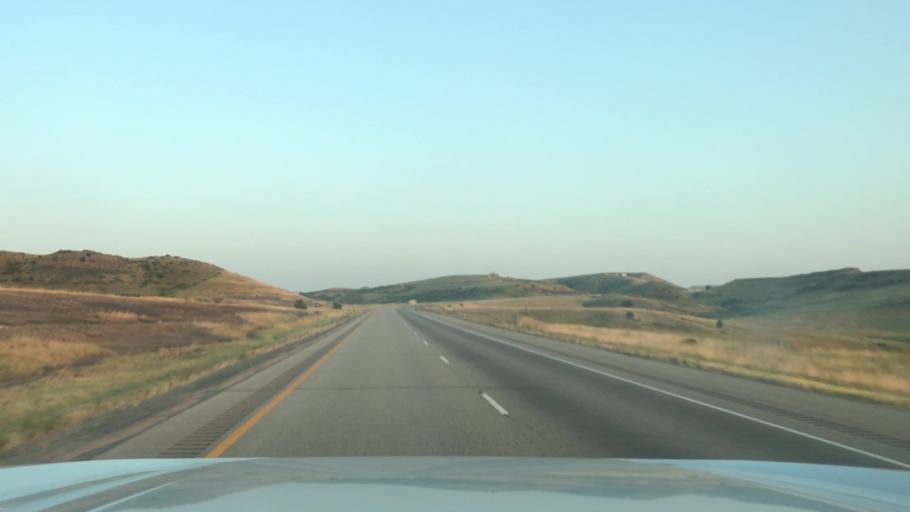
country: US
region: Wyoming
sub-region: Sheridan County
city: Sheridan
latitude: 44.7436
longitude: -106.9227
